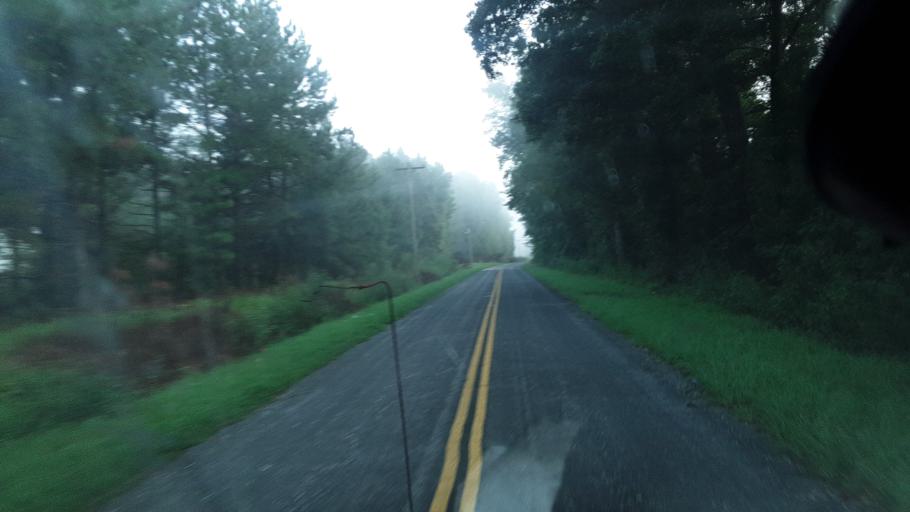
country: US
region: South Carolina
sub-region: Williamsburg County
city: Kingstree
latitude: 33.8157
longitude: -79.9630
